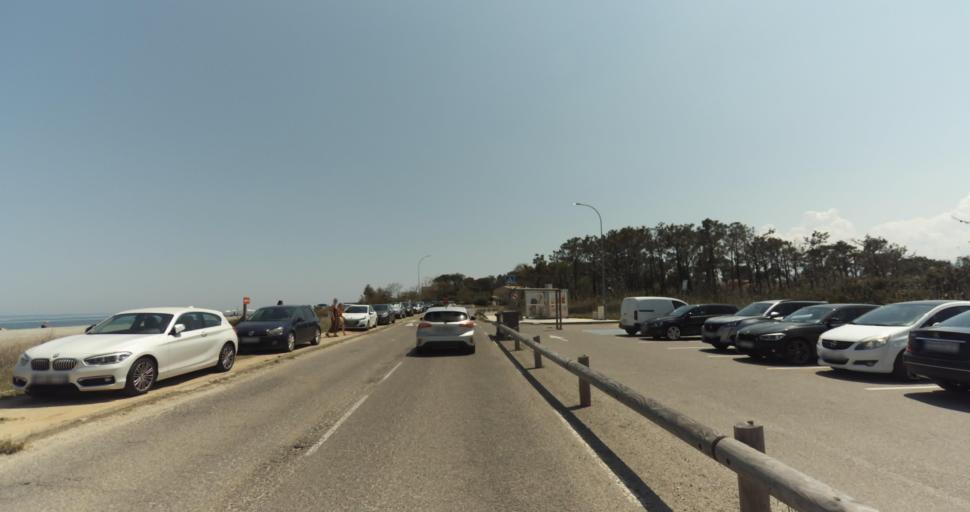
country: FR
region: Corsica
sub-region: Departement de la Haute-Corse
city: Biguglia
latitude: 42.6414
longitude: 9.4604
